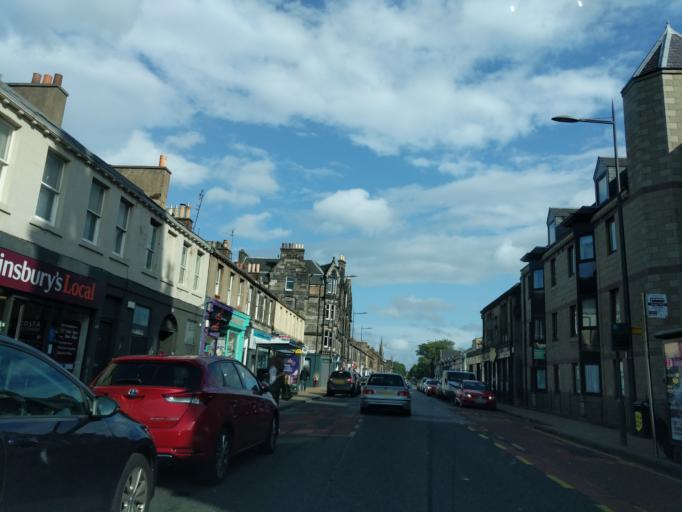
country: GB
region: Scotland
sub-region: West Lothian
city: Seafield
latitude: 55.9522
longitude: -3.1122
